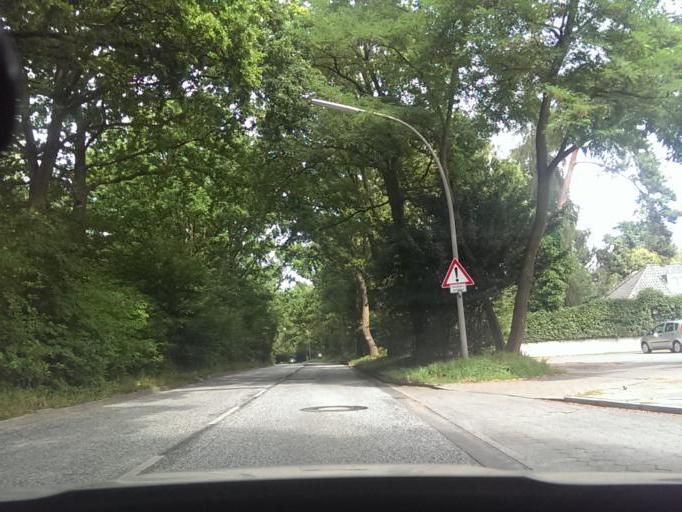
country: DE
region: Hamburg
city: Lemsahl-Mellingstedt
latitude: 53.6756
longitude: 10.0931
